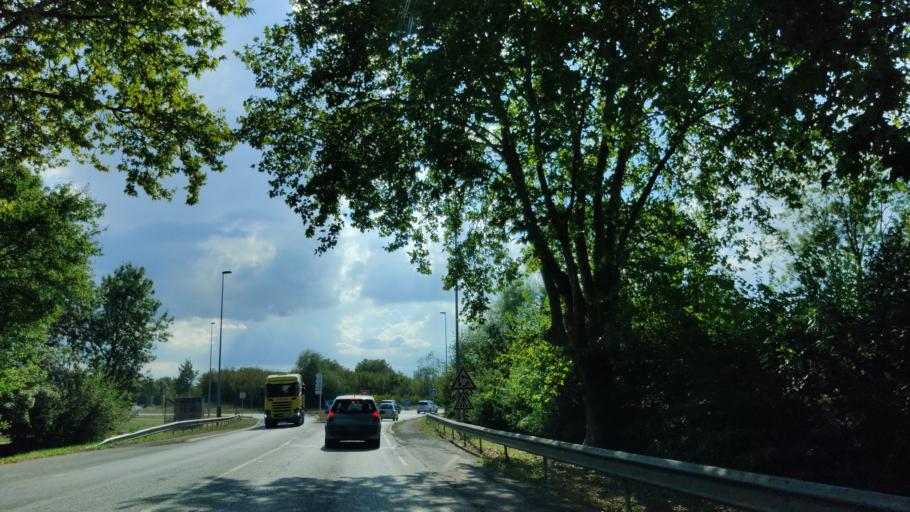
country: FR
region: Poitou-Charentes
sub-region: Departement des Deux-Sevres
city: Bessines
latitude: 46.3036
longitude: -0.4906
